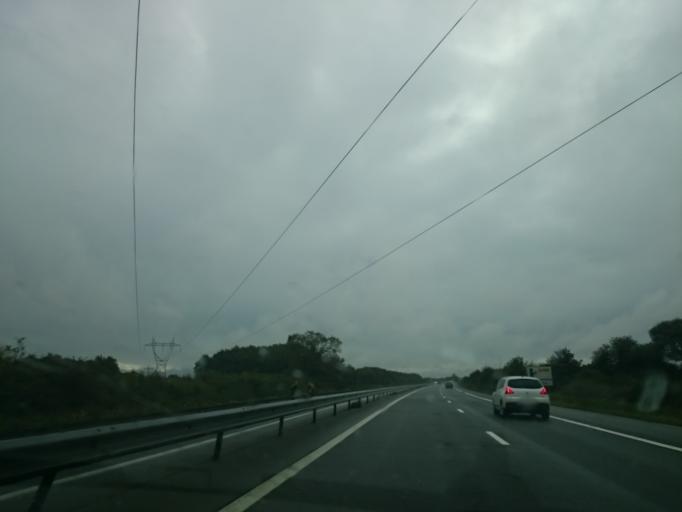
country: FR
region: Pays de la Loire
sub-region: Departement de la Loire-Atlantique
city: Prinquiau
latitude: 47.4044
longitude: -2.0105
